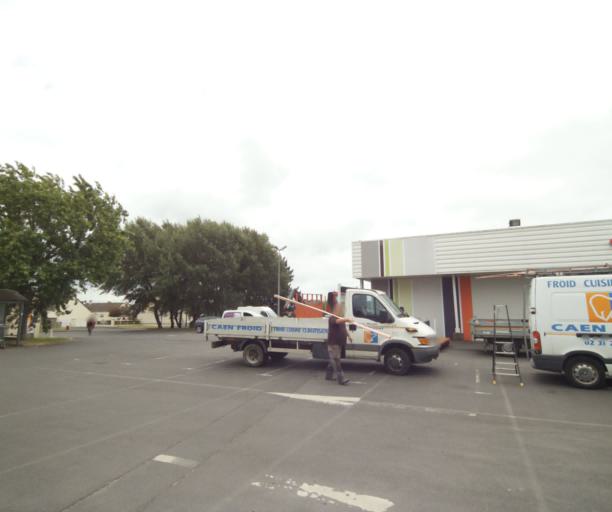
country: FR
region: Lower Normandy
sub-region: Departement du Calvados
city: Dives-sur-Mer
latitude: 49.2849
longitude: -0.1079
